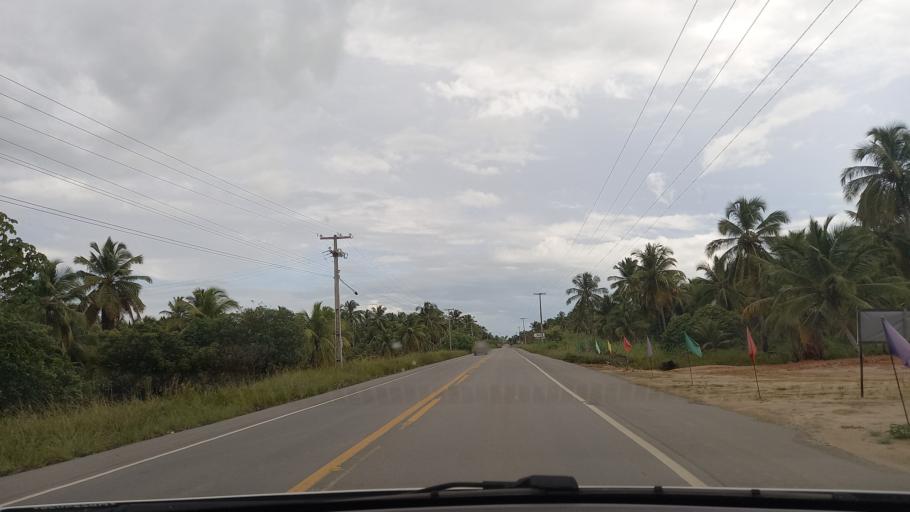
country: BR
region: Alagoas
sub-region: Maragogi
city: Maragogi
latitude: -8.9616
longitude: -35.1803
